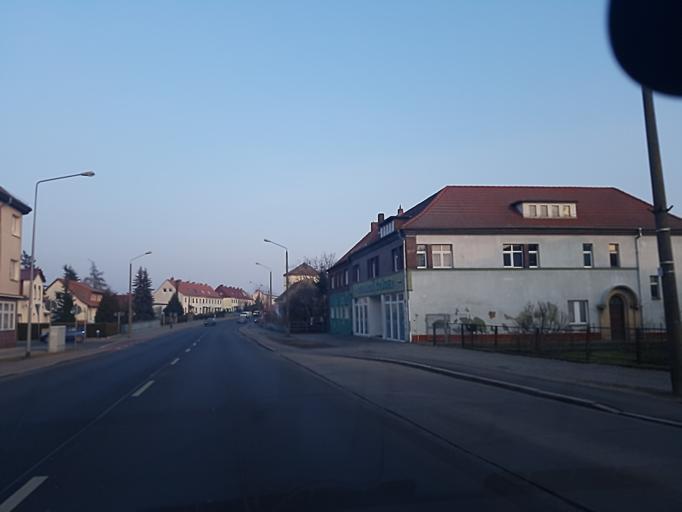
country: DE
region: Saxony-Anhalt
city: Wittenburg
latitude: 51.8675
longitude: 12.6014
